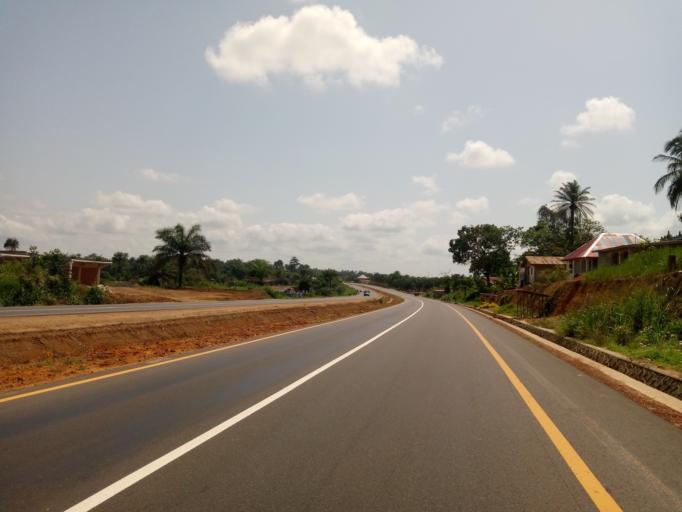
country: SL
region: Western Area
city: Waterloo
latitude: 8.3652
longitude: -12.9621
